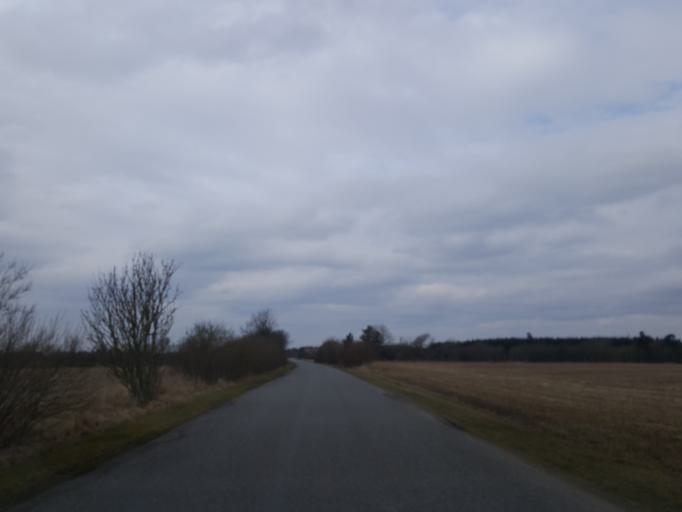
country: DK
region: Central Jutland
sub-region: Holstebro Kommune
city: Ulfborg
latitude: 56.3598
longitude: 8.2614
